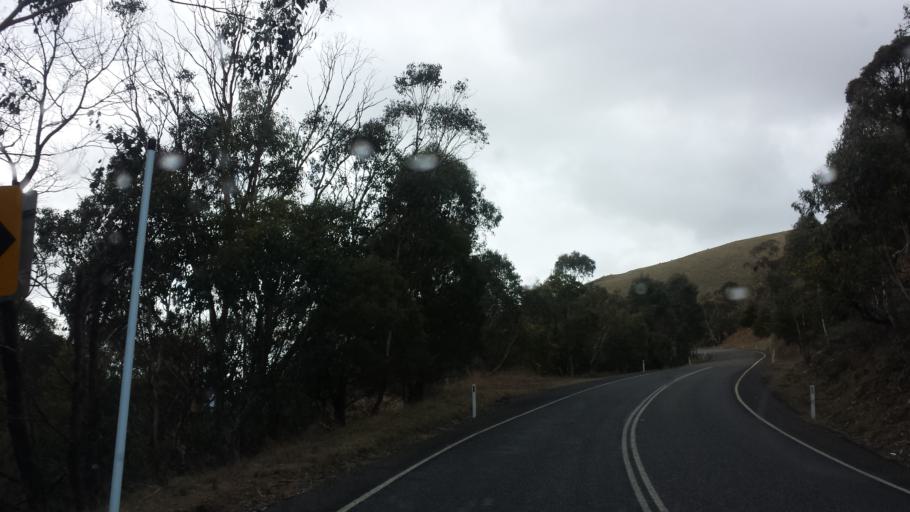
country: AU
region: Victoria
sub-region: Alpine
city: Mount Beauty
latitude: -37.1184
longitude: 147.5517
